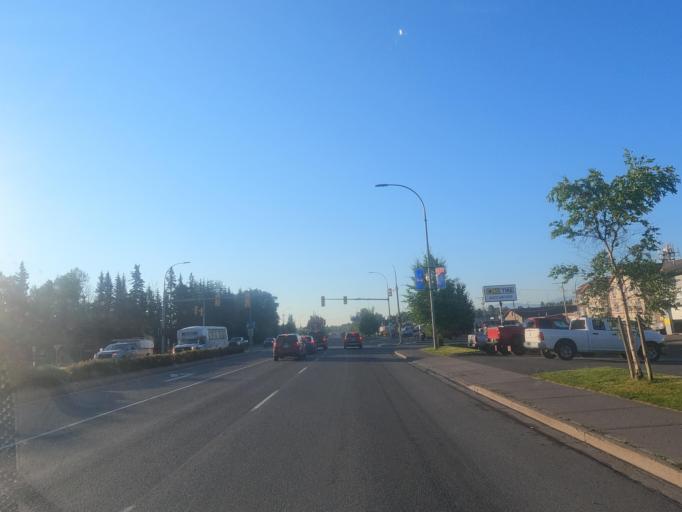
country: CA
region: British Columbia
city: Smithers
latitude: 54.7837
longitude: -127.1697
